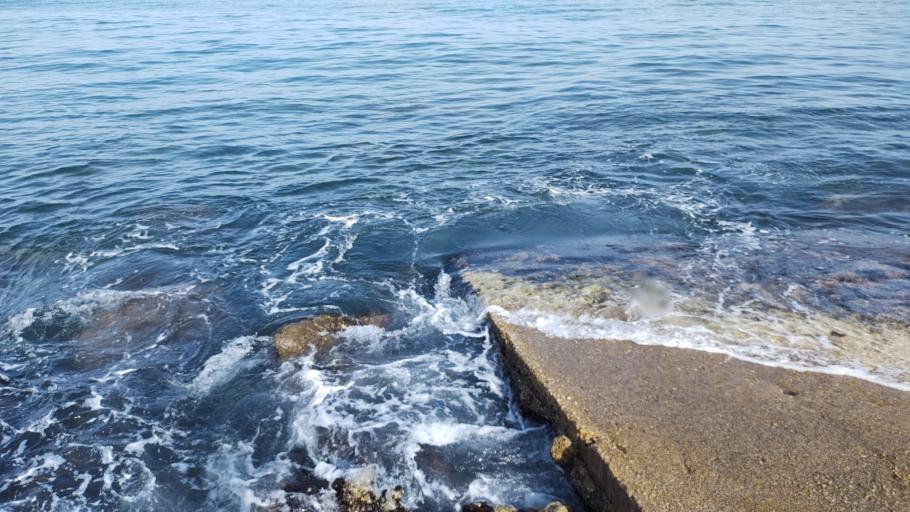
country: ES
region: Andalusia
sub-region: Provincia de Malaga
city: Benalmadena
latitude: 36.5787
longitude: -4.5389
